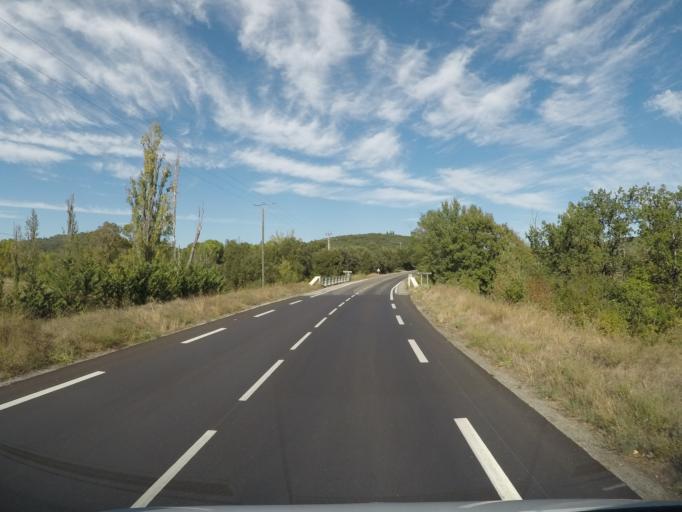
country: FR
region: Languedoc-Roussillon
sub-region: Departement du Gard
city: Sauve
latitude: 43.9764
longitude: 3.9249
